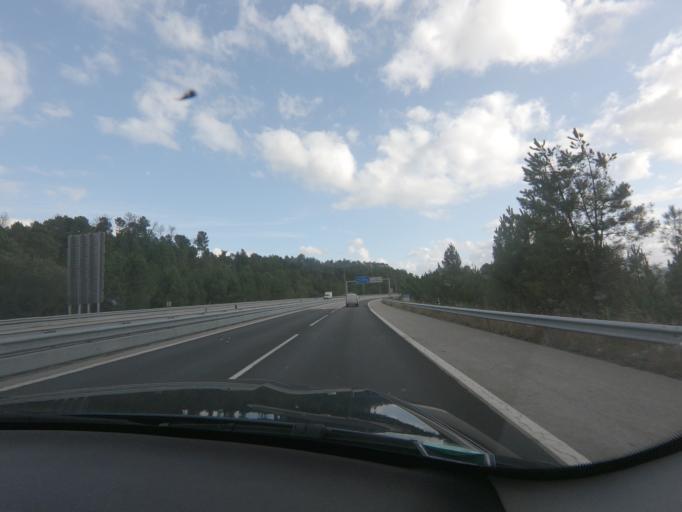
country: PT
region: Viseu
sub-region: Castro Daire
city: Castro Daire
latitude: 40.8655
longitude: -7.9273
